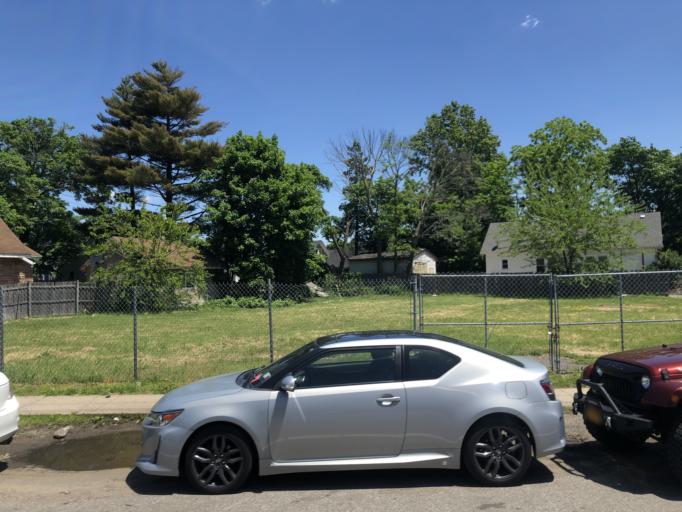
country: US
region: New York
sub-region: Nassau County
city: Roosevelt
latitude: 40.6740
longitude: -73.5825
